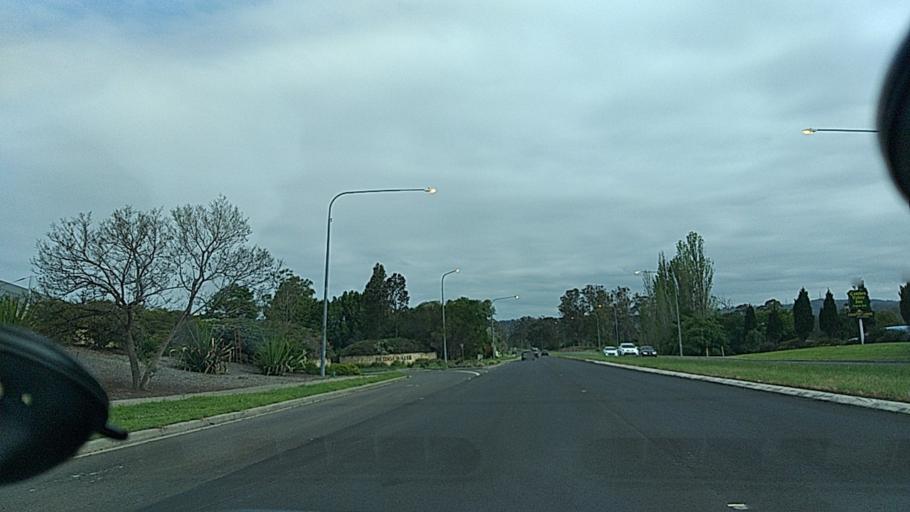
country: AU
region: New South Wales
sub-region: Camden
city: Camden South
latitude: -34.0917
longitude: 150.6951
